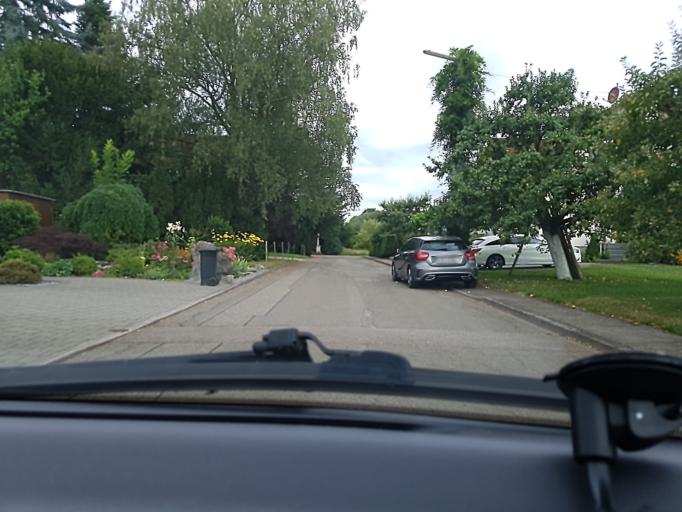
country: DE
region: Baden-Wuerttemberg
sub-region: Freiburg Region
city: Offenburg
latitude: 48.4851
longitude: 7.9107
